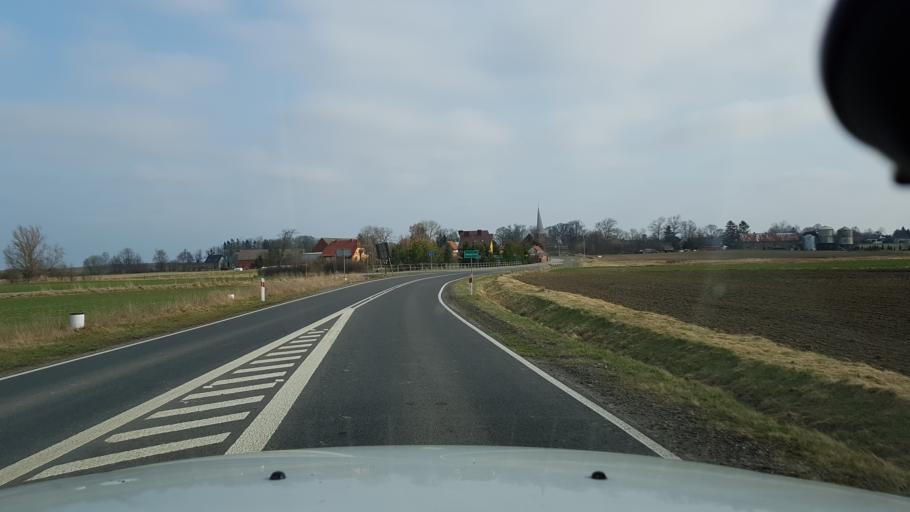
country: PL
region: West Pomeranian Voivodeship
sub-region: Powiat koszalinski
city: Sianow
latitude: 54.2910
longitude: 16.2725
